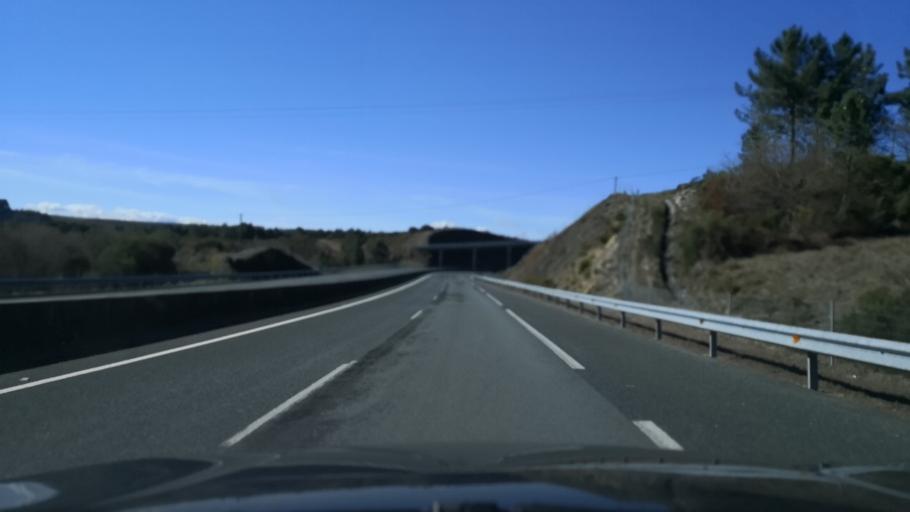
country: ES
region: Galicia
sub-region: Provincia de Pontevedra
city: Dozon
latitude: 42.5878
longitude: -8.0768
